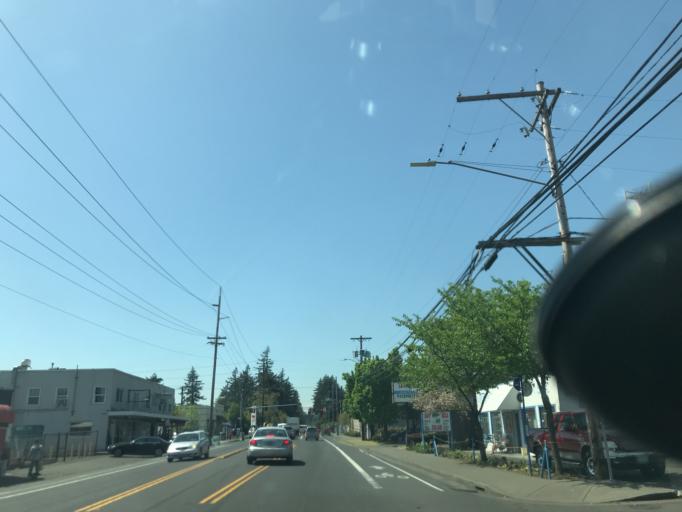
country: US
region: Oregon
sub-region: Multnomah County
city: Lents
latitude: 45.4972
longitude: -122.5359
